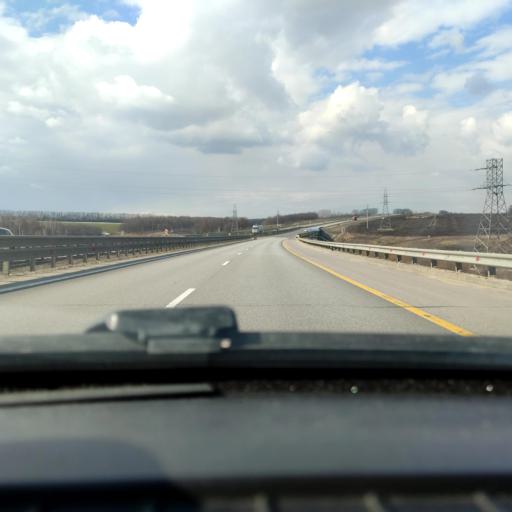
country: RU
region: Tula
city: Kazachka
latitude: 53.2736
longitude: 38.1824
